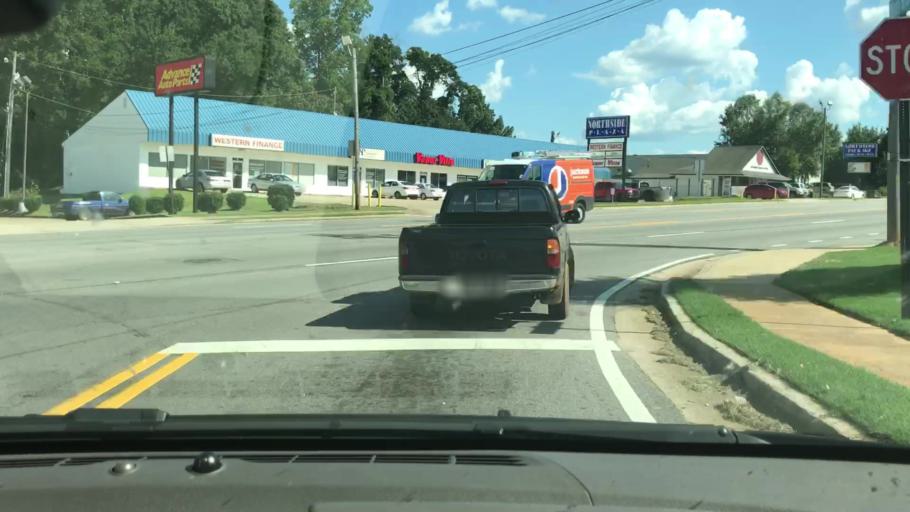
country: US
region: Georgia
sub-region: Troup County
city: La Grange
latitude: 33.0517
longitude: -85.0289
